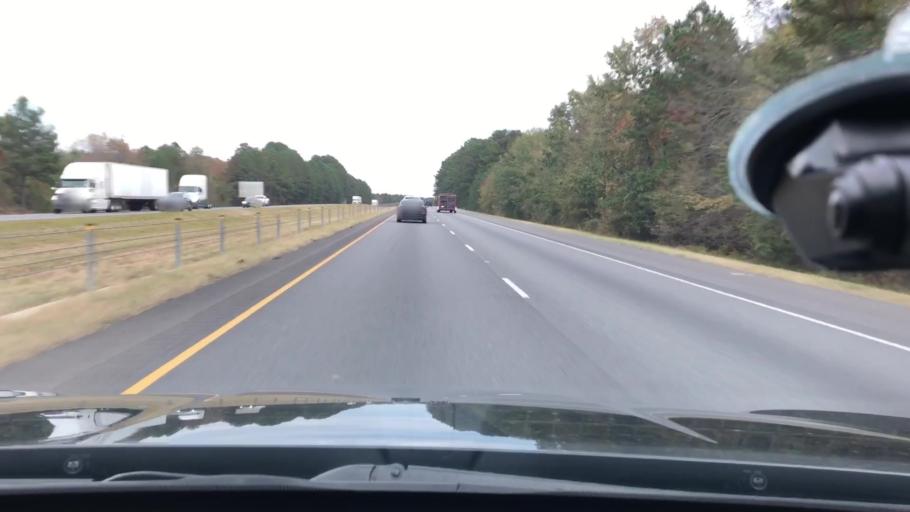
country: US
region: Arkansas
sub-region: Clark County
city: Arkadelphia
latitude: 34.2000
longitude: -93.0510
